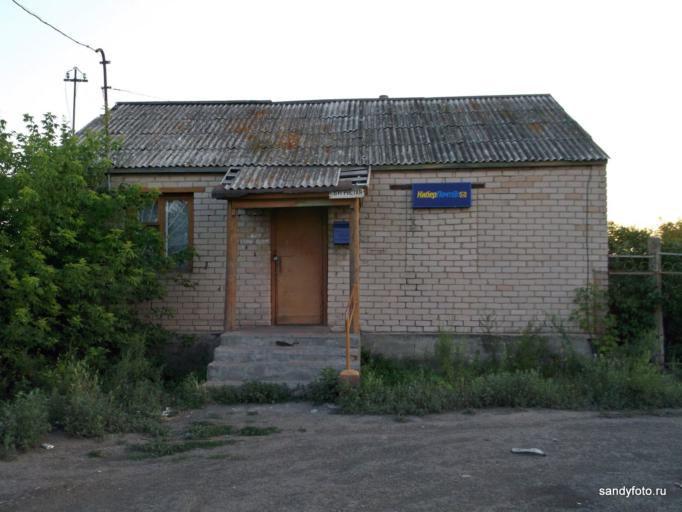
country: RU
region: Chelyabinsk
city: Troitsk
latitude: 54.0459
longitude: 61.6062
